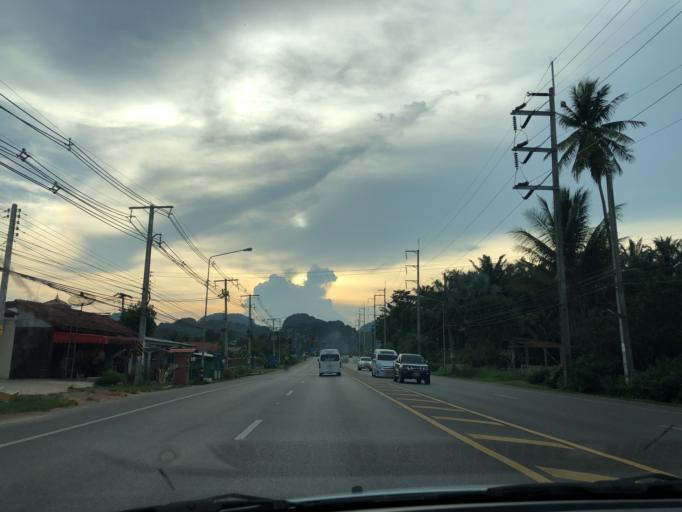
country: TH
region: Krabi
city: Krabi
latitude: 8.0829
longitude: 98.8909
